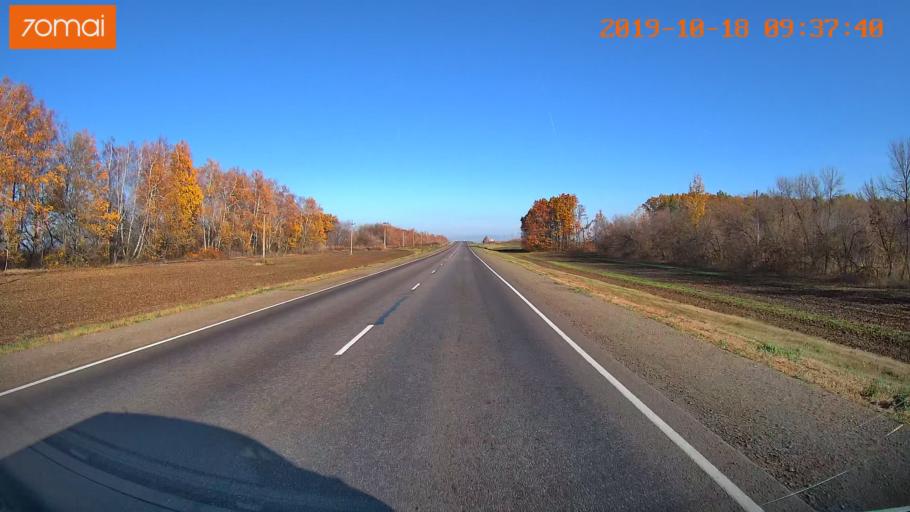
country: RU
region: Tula
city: Yefremov
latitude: 53.2258
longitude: 38.1401
